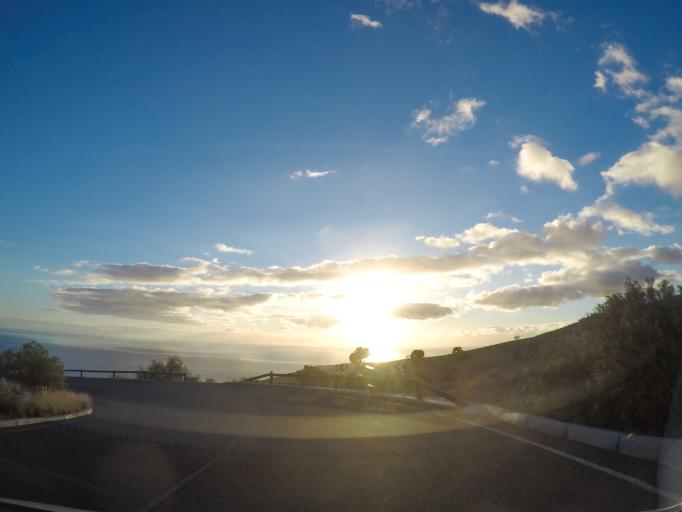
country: ES
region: Canary Islands
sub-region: Provincia de Santa Cruz de Tenerife
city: Alajero
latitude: 28.0348
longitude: -17.2214
